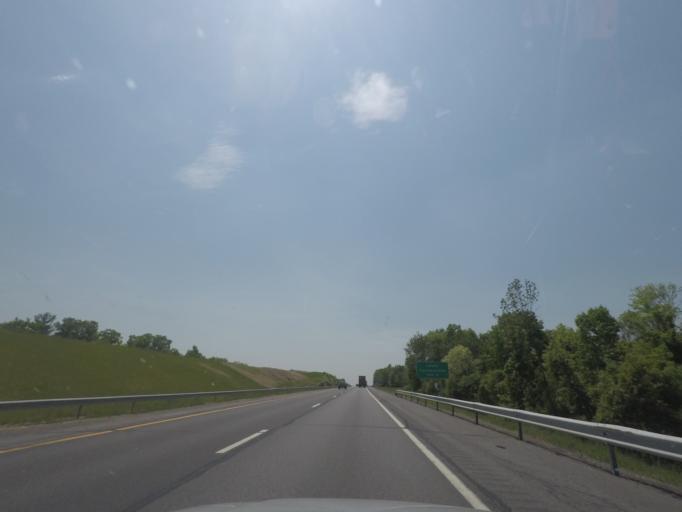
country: US
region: New York
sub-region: Greene County
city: Jefferson Heights
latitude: 42.2712
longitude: -73.8747
